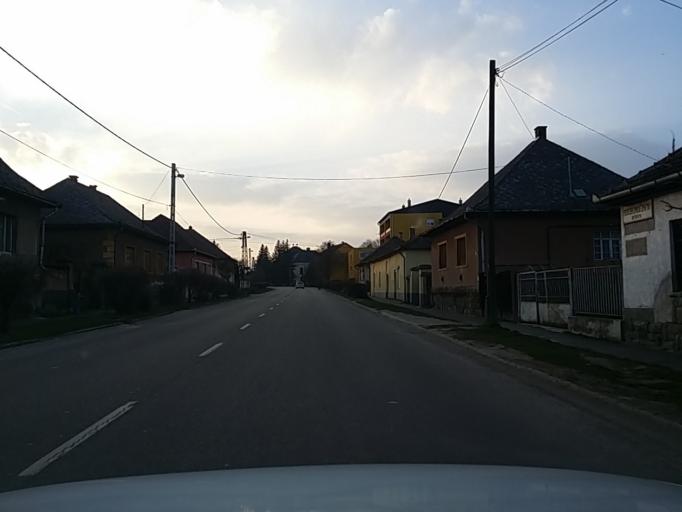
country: HU
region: Heves
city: Petervasara
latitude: 48.0183
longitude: 20.1006
